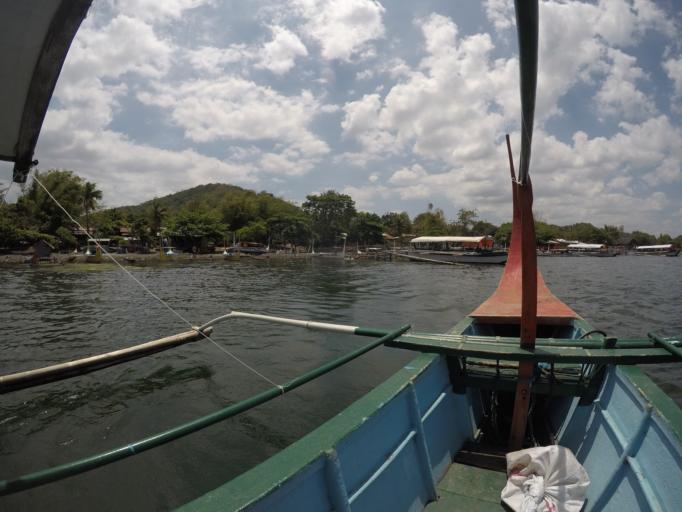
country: PH
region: Calabarzon
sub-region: Province of Batangas
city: Talisay
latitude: 14.0353
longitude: 121.0039
